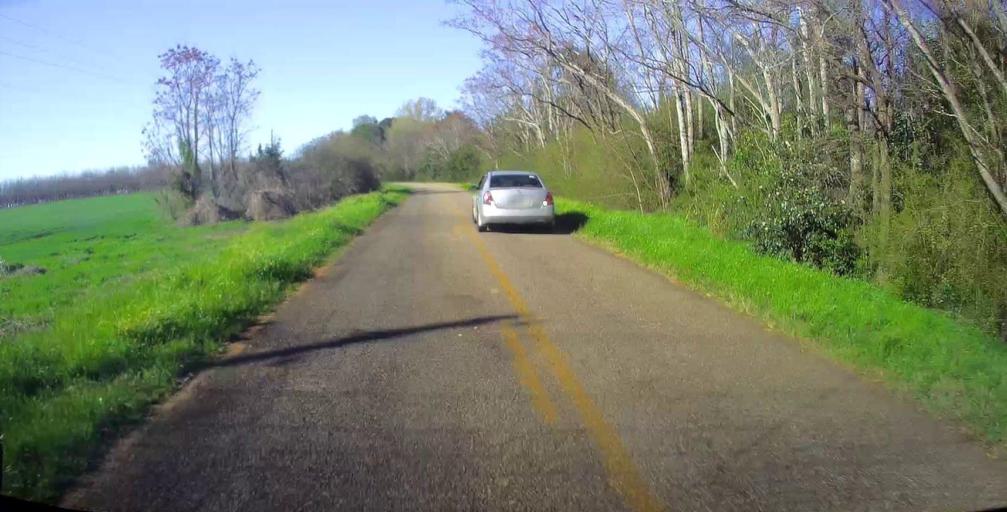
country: US
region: Georgia
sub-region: Macon County
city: Marshallville
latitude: 32.4909
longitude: -83.9519
